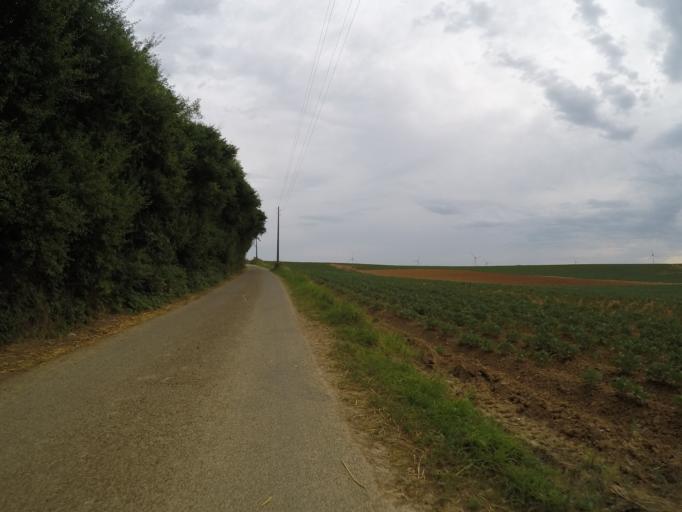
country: BE
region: Wallonia
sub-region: Province de Namur
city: Assesse
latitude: 50.3121
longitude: 5.0051
